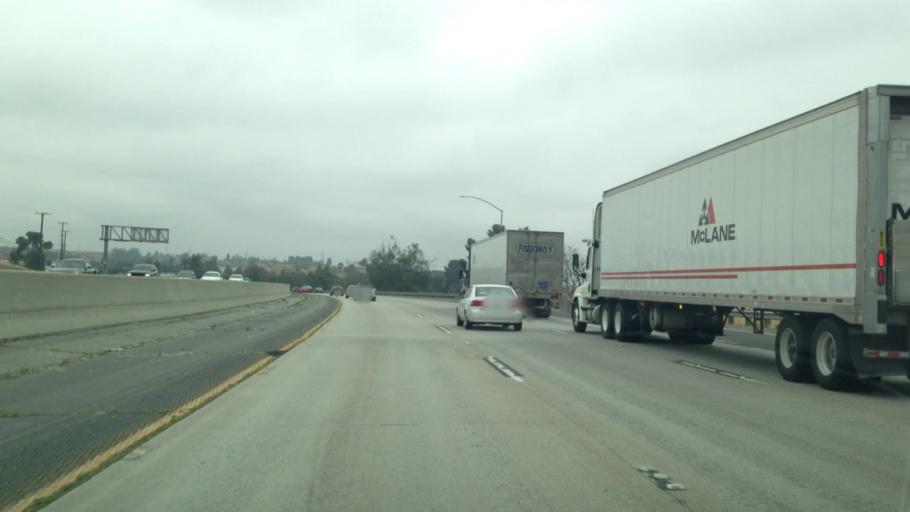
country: US
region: California
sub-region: Riverside County
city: Calimesa
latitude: 33.9767
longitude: -117.0484
